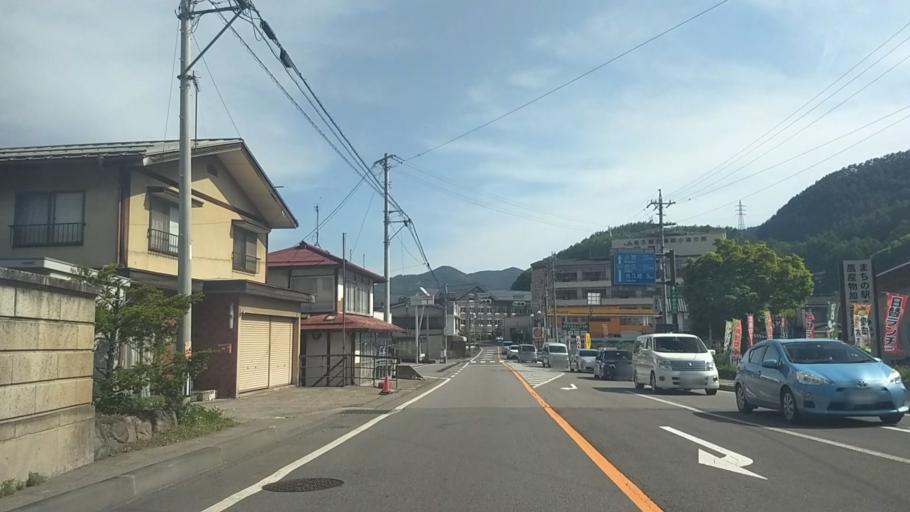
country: JP
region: Nagano
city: Saku
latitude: 36.0926
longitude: 138.4828
